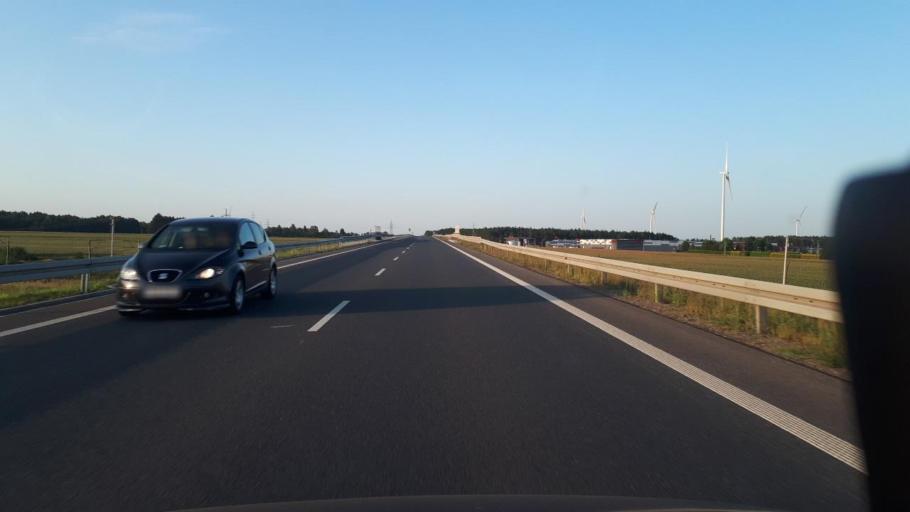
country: PL
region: Greater Poland Voivodeship
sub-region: Powiat kepinski
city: Baranow
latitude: 51.2662
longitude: 18.0222
